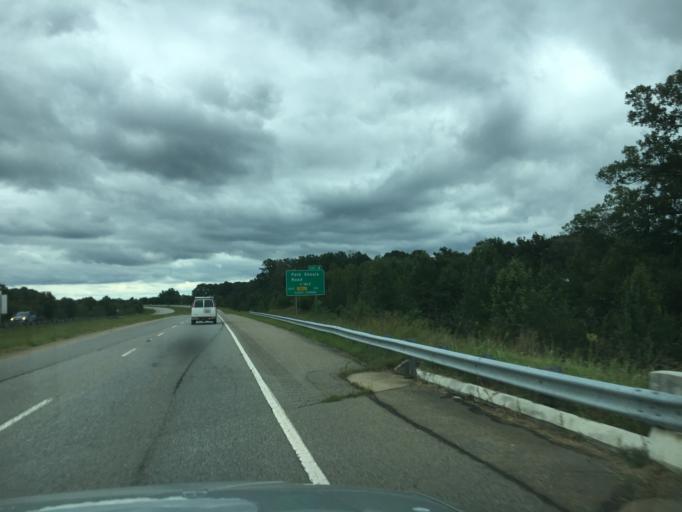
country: US
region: South Carolina
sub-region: Greenville County
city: Golden Grove
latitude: 34.7200
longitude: -82.3669
